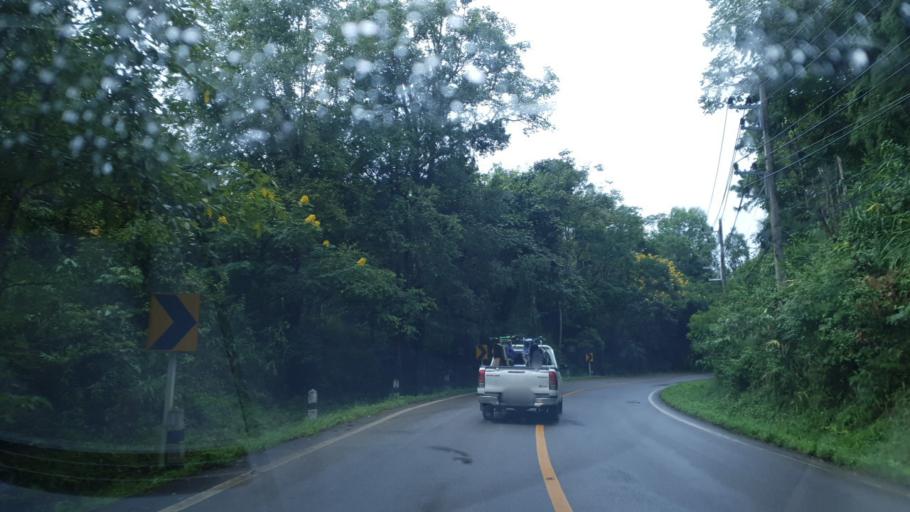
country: TH
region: Mae Hong Son
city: Ban Huai I Huak
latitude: 18.1614
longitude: 98.0498
